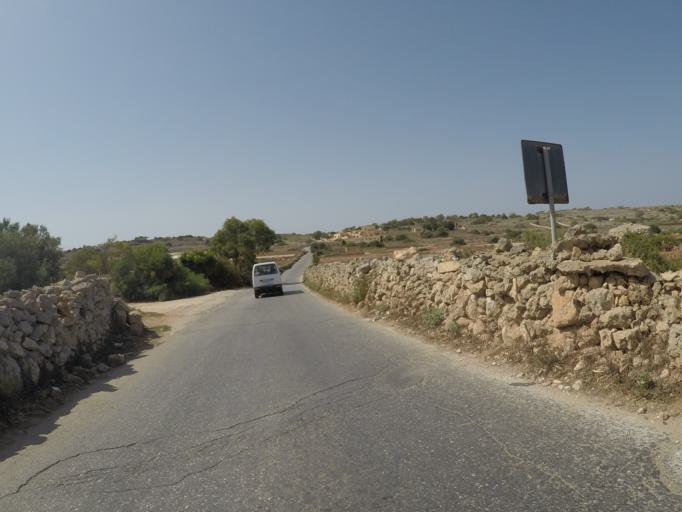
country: MT
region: L-Imgarr
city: Imgarr
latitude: 35.9245
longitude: 14.3794
